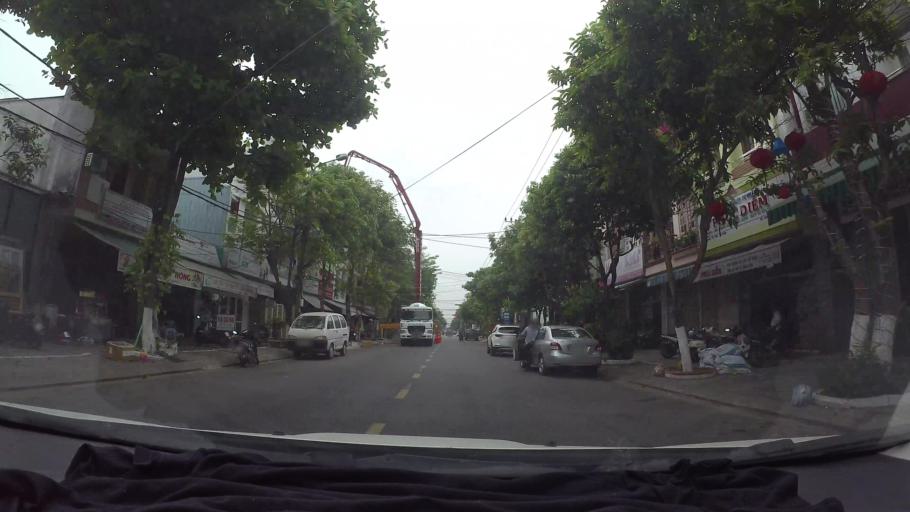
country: VN
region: Da Nang
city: Cam Le
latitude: 16.0373
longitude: 108.2141
